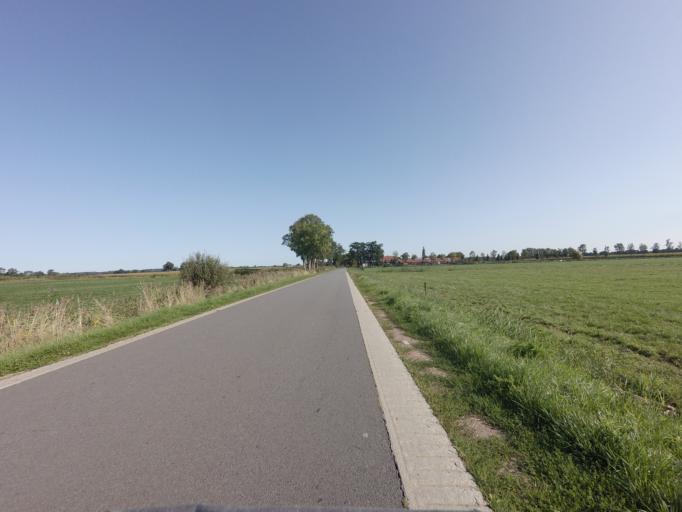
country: NL
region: Overijssel
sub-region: Gemeente Raalte
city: Raalte
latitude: 52.4081
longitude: 6.2850
